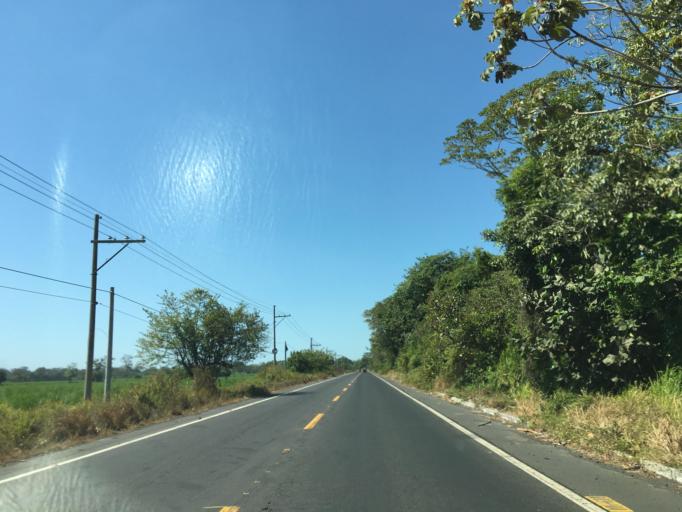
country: GT
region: Escuintla
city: Puerto San Jose
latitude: 14.0244
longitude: -90.8871
